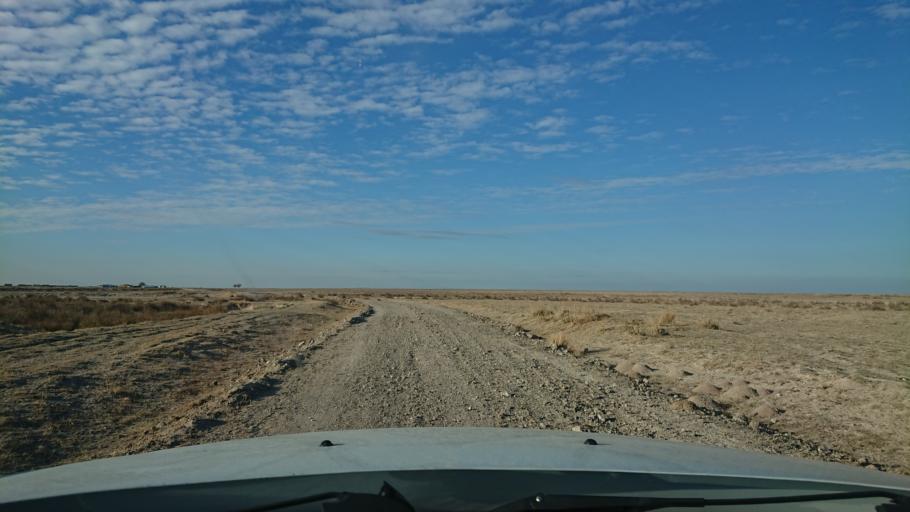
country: TR
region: Aksaray
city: Eskil
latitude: 38.5621
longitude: 33.3068
